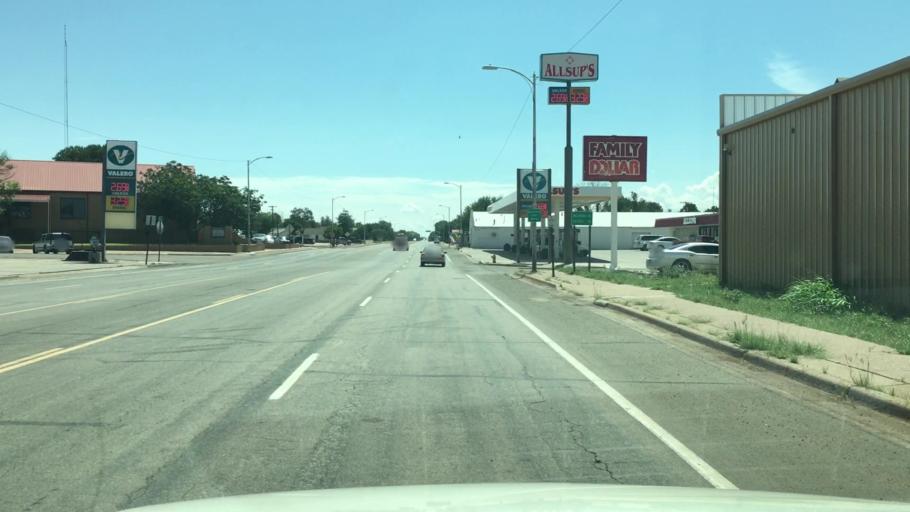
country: US
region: New Mexico
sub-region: De Baca County
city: Fort Sumner
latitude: 34.4711
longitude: -104.2438
